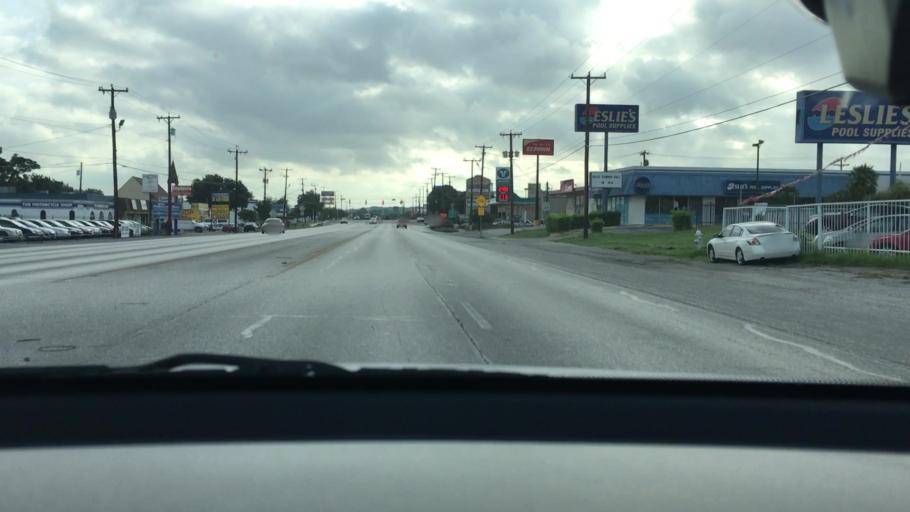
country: US
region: Texas
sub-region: Bexar County
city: Windcrest
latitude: 29.5091
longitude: -98.4093
